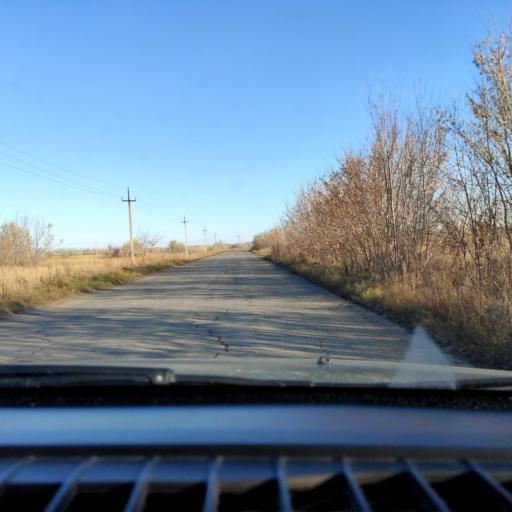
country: RU
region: Samara
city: Tol'yatti
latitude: 53.6417
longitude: 49.3152
